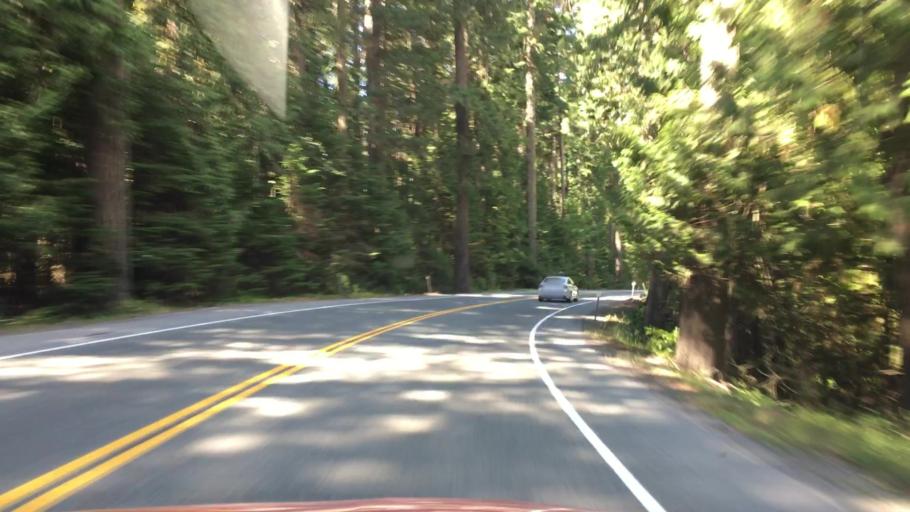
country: CA
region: British Columbia
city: Port Alberni
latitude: 49.2652
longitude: -124.6738
